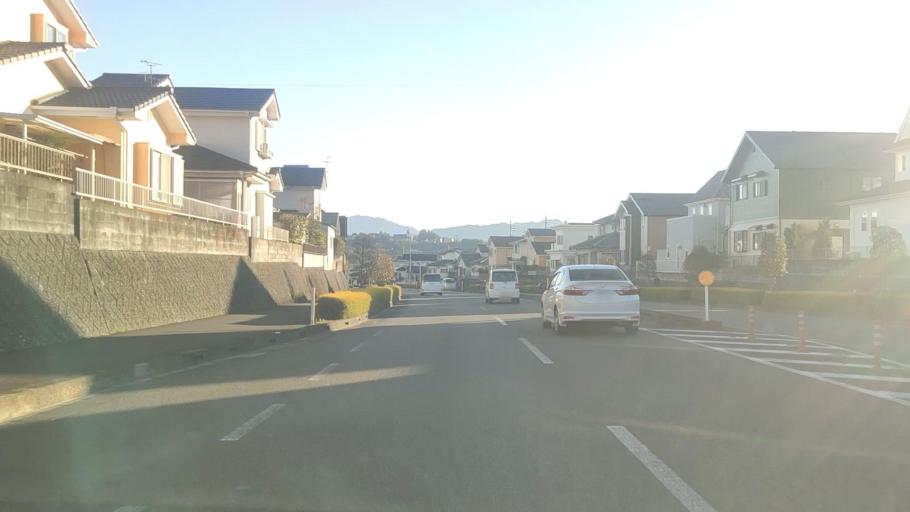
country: JP
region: Miyazaki
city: Miyazaki-shi
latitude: 31.8764
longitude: 131.3920
